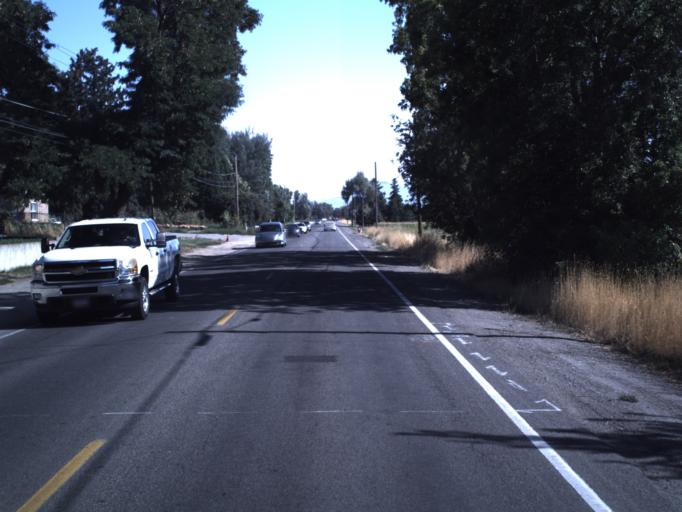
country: US
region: Utah
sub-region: Utah County
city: Orem
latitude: 40.2677
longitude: -111.7212
